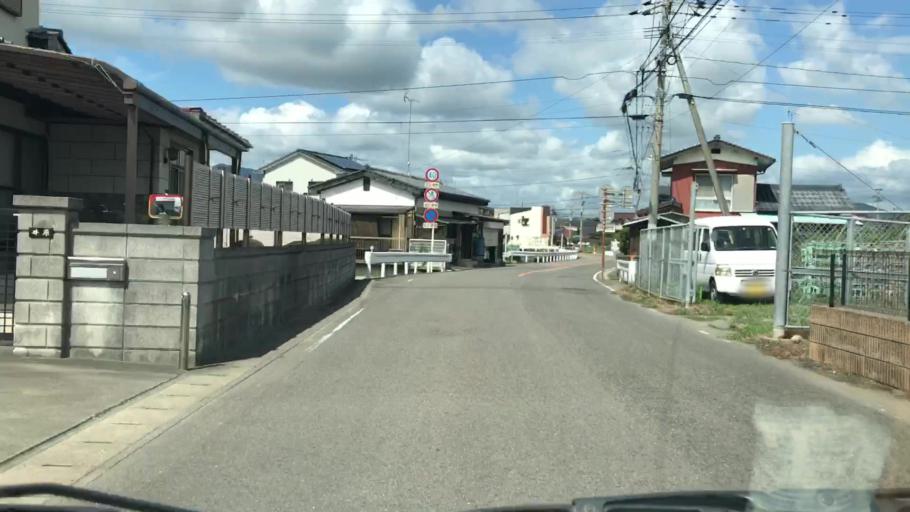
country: JP
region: Saga Prefecture
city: Saga-shi
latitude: 33.2434
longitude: 130.2021
